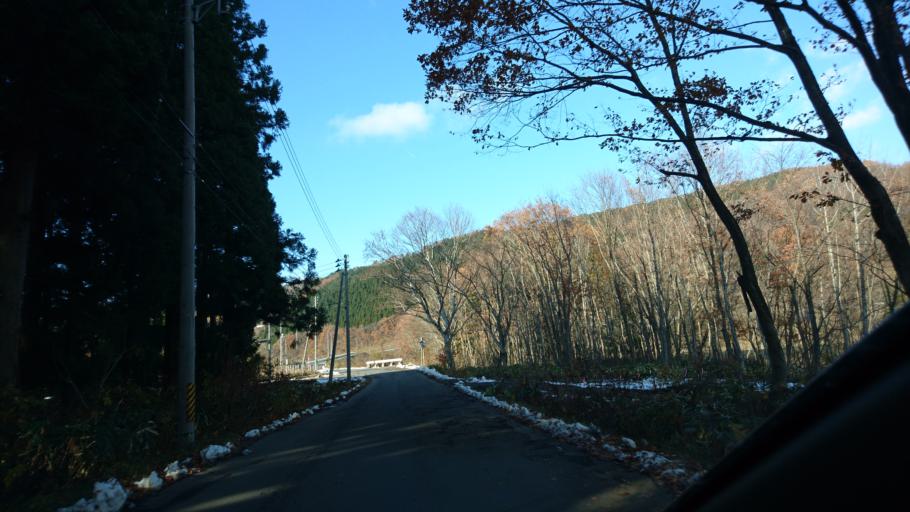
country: JP
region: Akita
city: Yokotemachi
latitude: 39.2988
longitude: 140.8294
